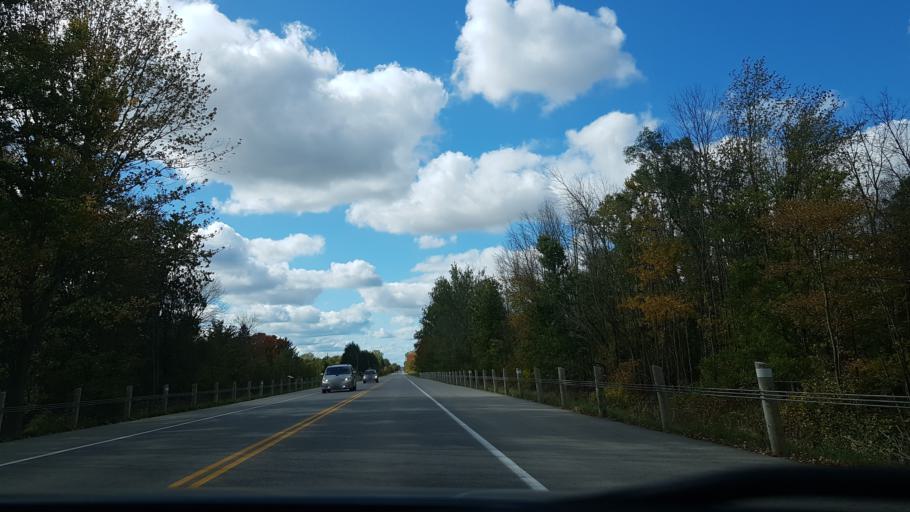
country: CA
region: Ontario
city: South Huron
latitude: 43.3555
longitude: -81.5428
